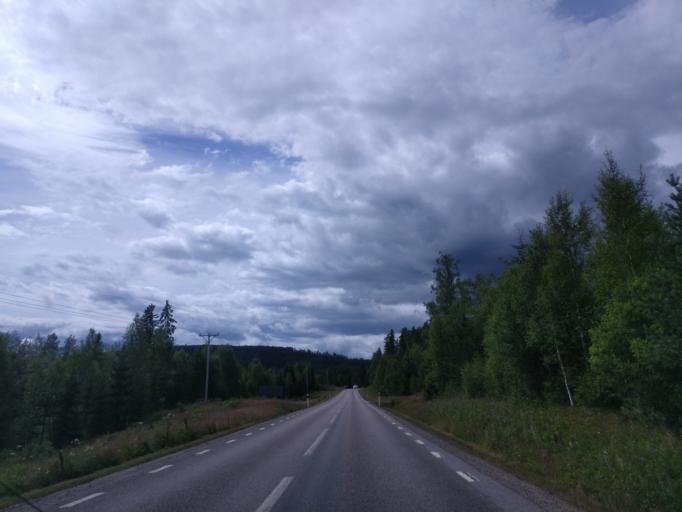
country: SE
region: Vaermland
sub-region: Hagfors Kommun
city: Ekshaerad
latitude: 60.1812
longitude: 13.3656
